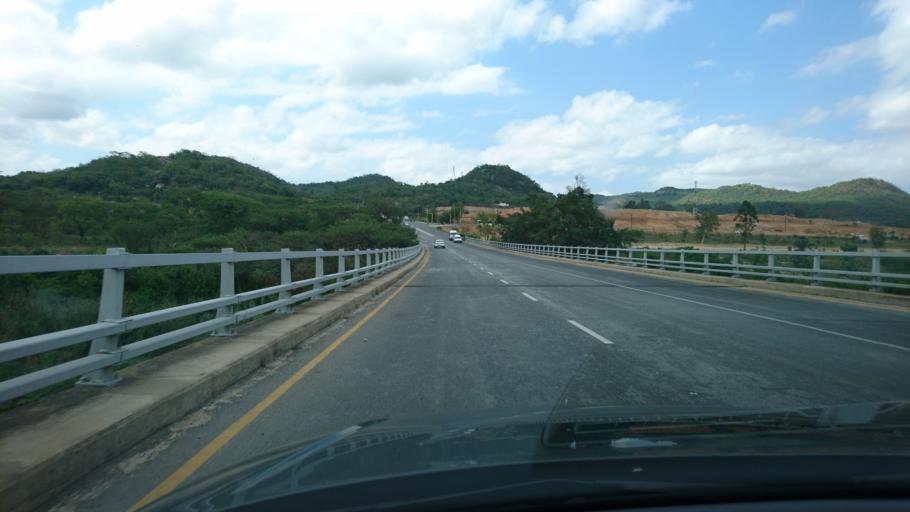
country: ZA
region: Mpumalanga
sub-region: Ehlanzeni District
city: Nelspruit
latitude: -25.4701
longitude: 31.0932
